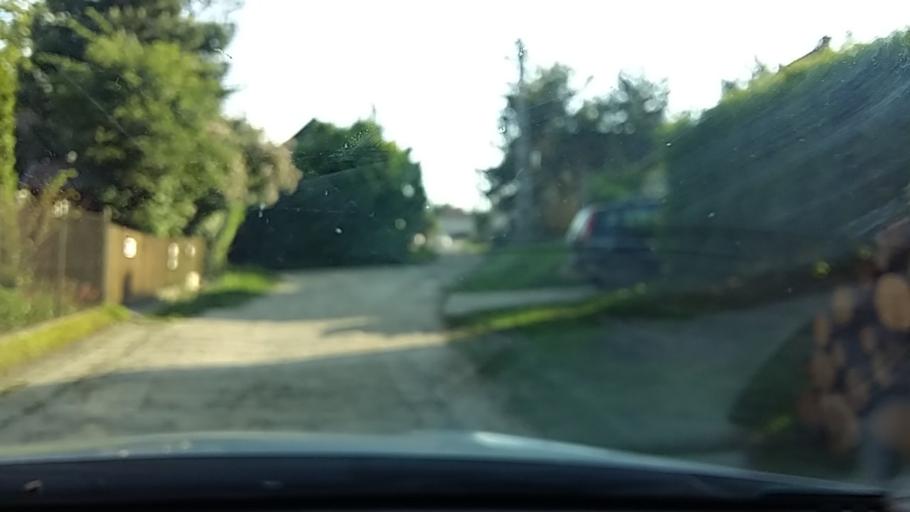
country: HU
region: Pest
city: Kosd
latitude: 47.8030
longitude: 19.2474
